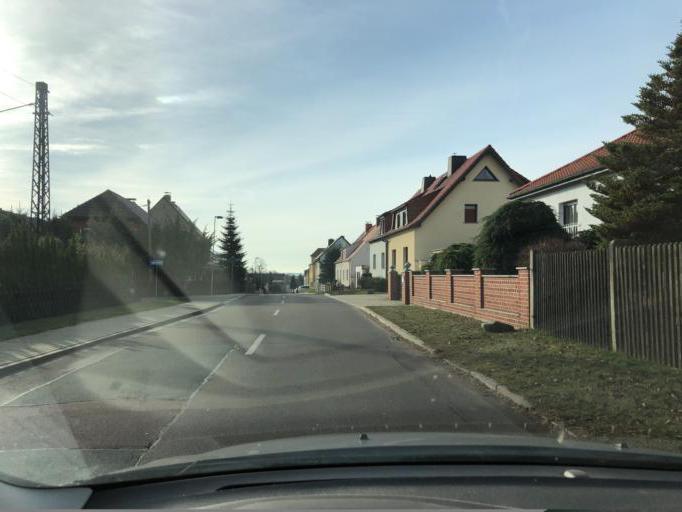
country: DE
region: Saxony-Anhalt
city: Reichardtswerben
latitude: 51.2421
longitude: 11.9509
